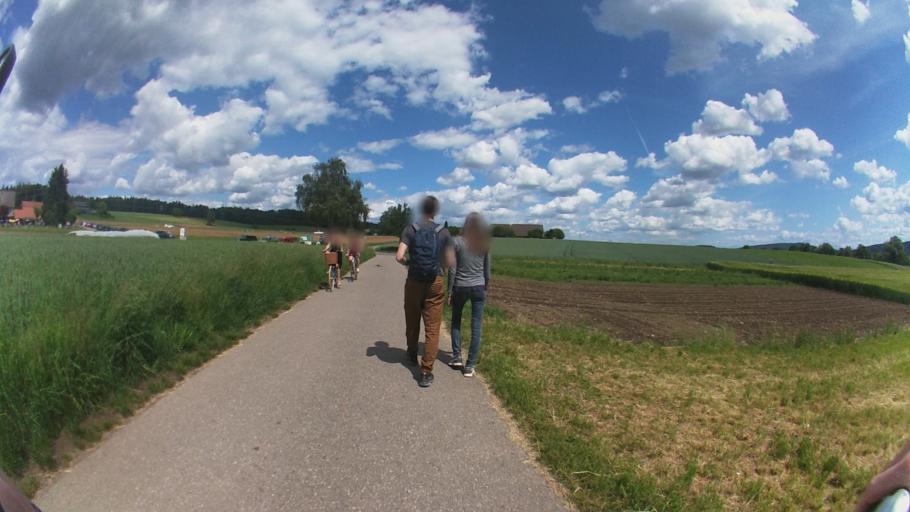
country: CH
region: Zurich
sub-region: Bezirk Zuerich
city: Zuerich (Kreis 11) / Affoltern
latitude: 47.4364
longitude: 8.5016
